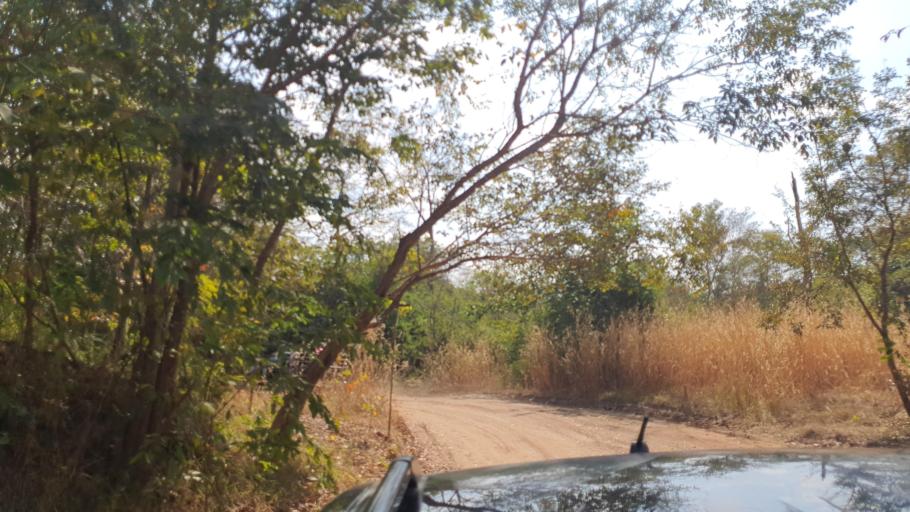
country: TH
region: Changwat Bueng Kan
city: Si Wilai
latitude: 18.2698
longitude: 103.7993
